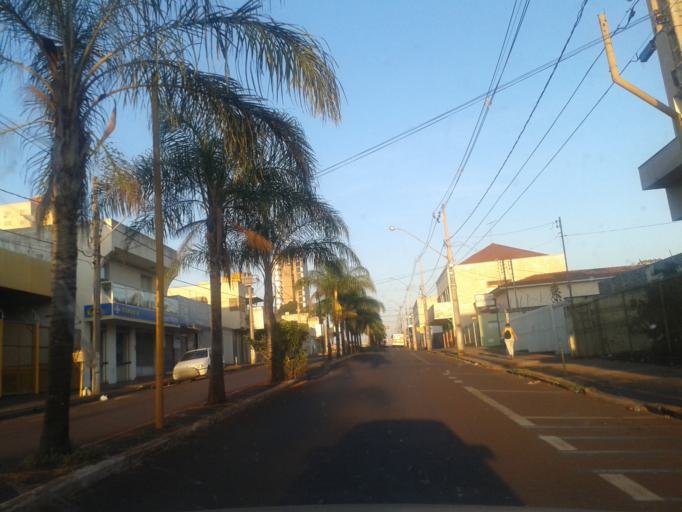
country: BR
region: Minas Gerais
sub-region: Ituiutaba
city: Ituiutaba
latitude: -18.9742
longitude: -49.4581
